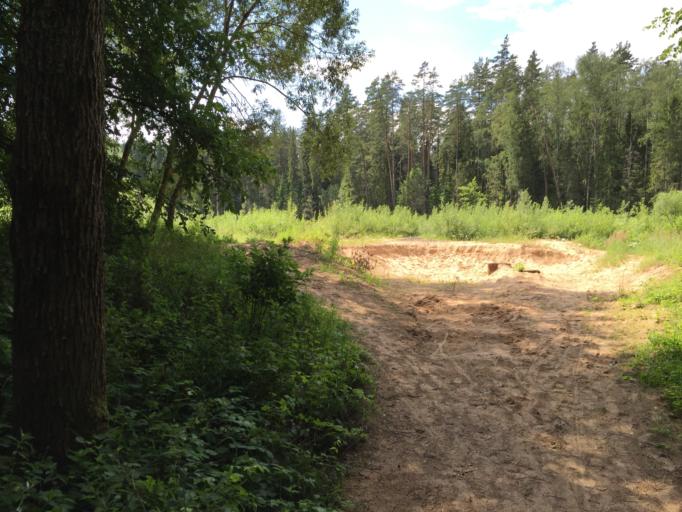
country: LV
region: Ligatne
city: Ligatne
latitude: 57.2553
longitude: 25.0621
